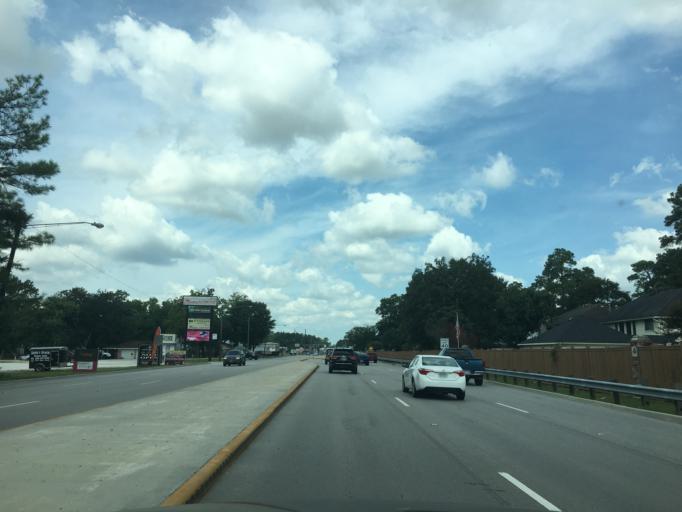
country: US
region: Texas
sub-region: Harris County
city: Spring
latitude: 30.1243
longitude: -95.4142
